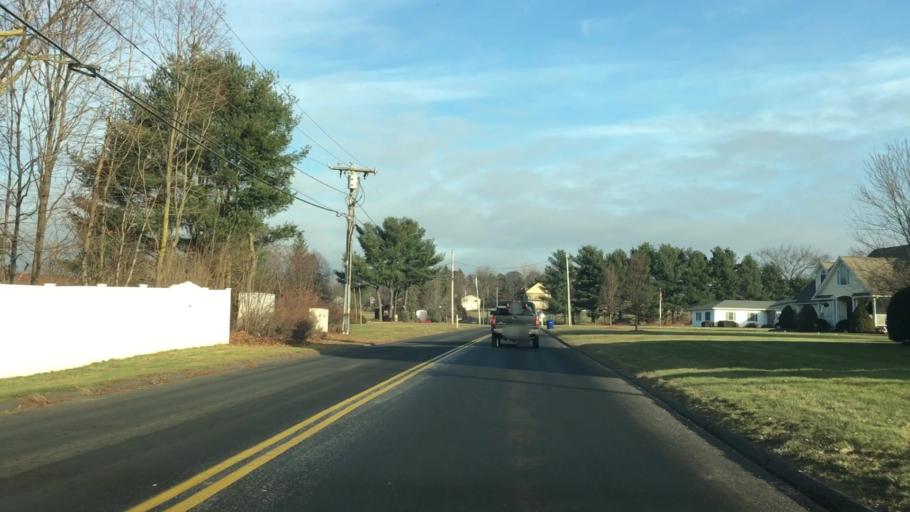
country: US
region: Connecticut
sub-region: Tolland County
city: Ellington
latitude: 41.9175
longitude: -72.4752
